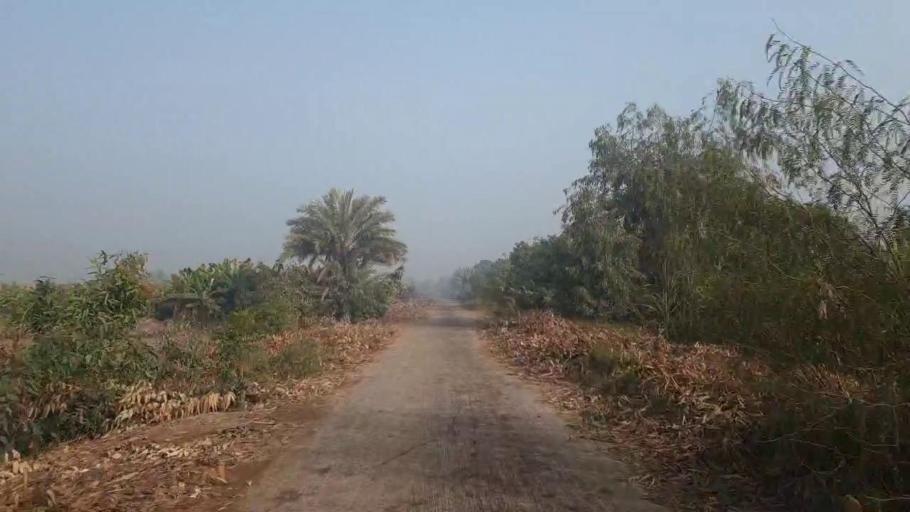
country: PK
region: Sindh
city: Tando Adam
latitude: 25.7994
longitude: 68.6334
